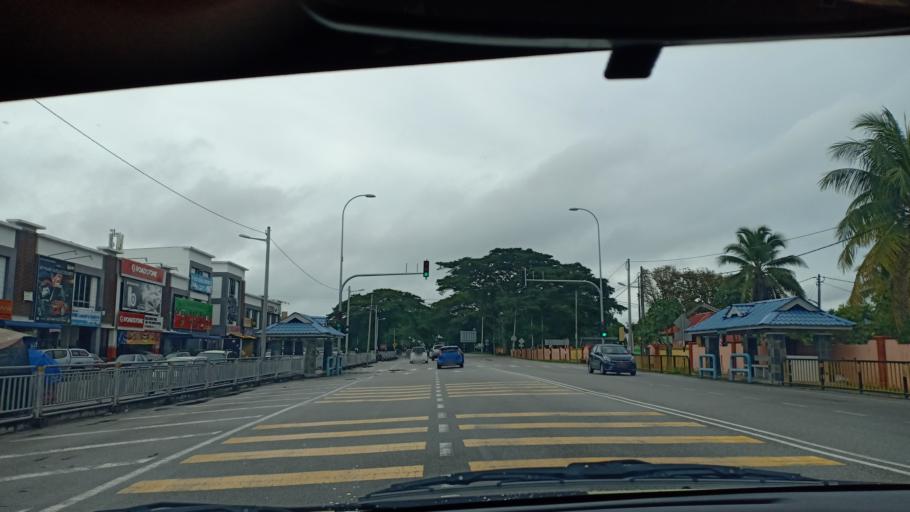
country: MY
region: Penang
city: Kepala Batas
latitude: 5.4898
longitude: 100.4574
